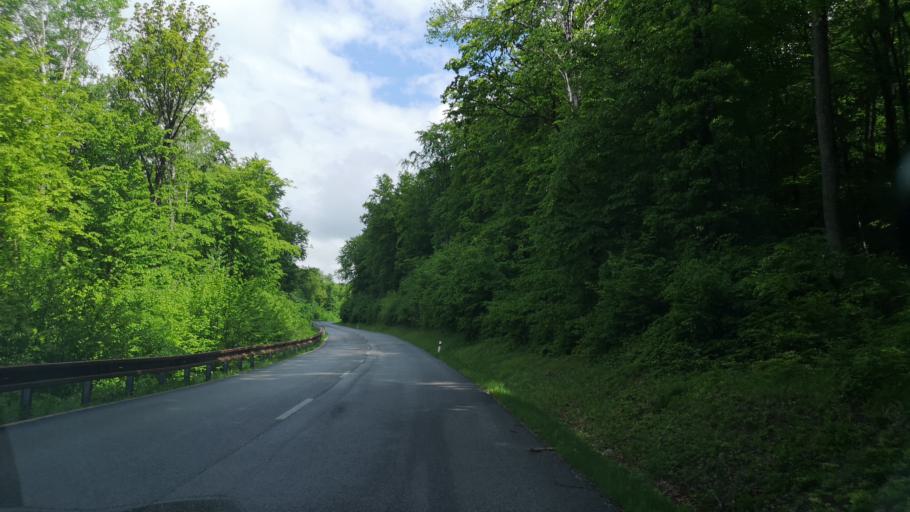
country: SK
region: Banskobystricky
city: Revuca
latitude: 48.6314
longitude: 20.2885
